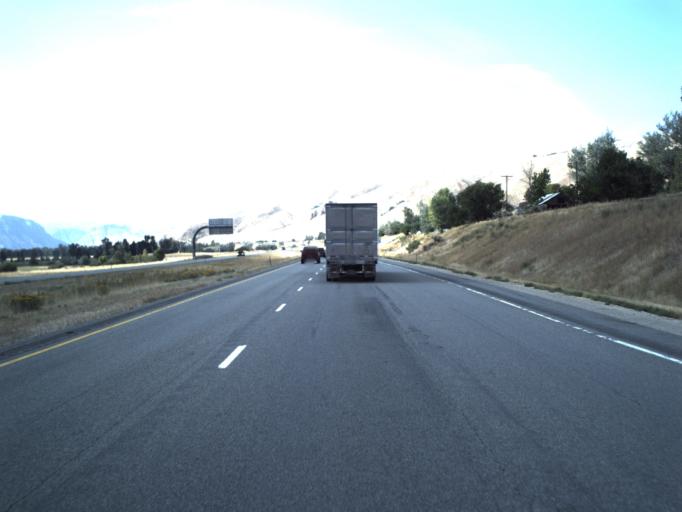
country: US
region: Utah
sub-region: Summit County
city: Coalville
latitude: 40.9745
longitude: -111.4438
